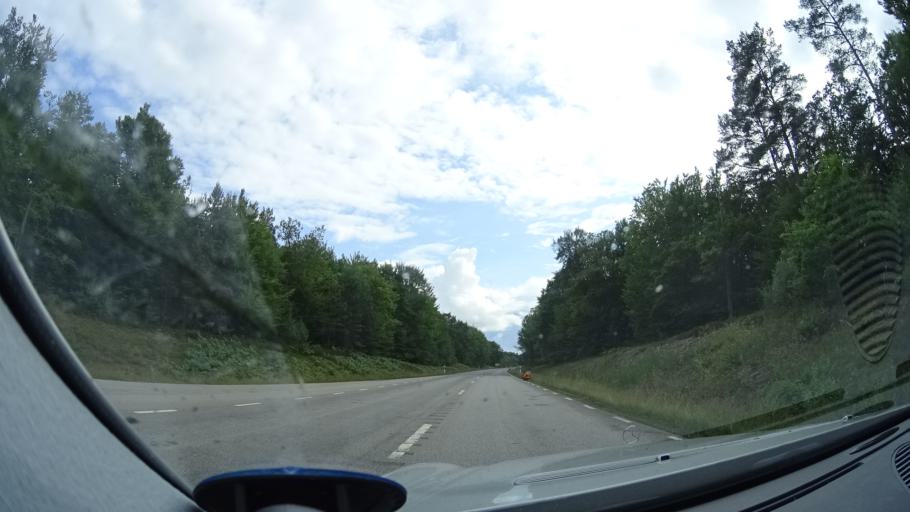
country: SE
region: Blekinge
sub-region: Karlshamns Kommun
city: Svangsta
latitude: 56.2334
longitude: 14.8255
